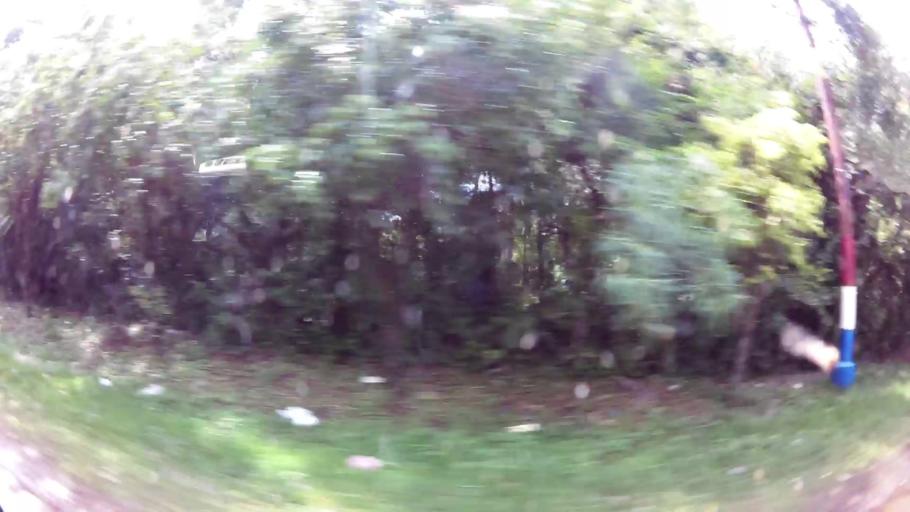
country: PY
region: Central
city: Limpio
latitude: -25.1830
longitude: -57.4514
